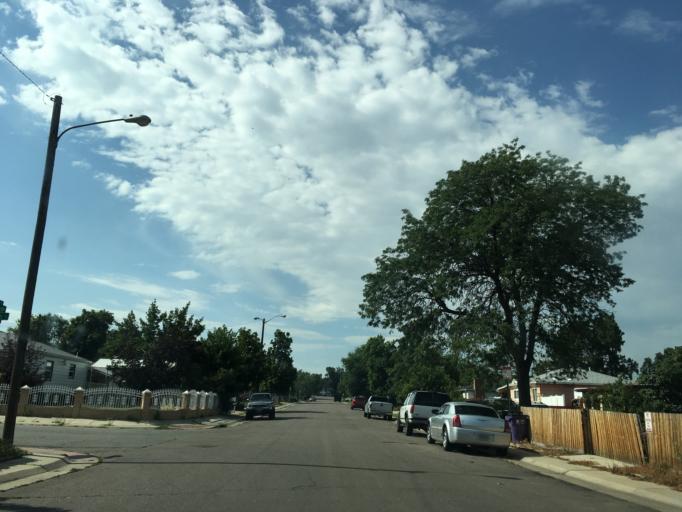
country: US
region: Colorado
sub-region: Jefferson County
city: Lakewood
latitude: 39.7035
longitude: -105.0409
